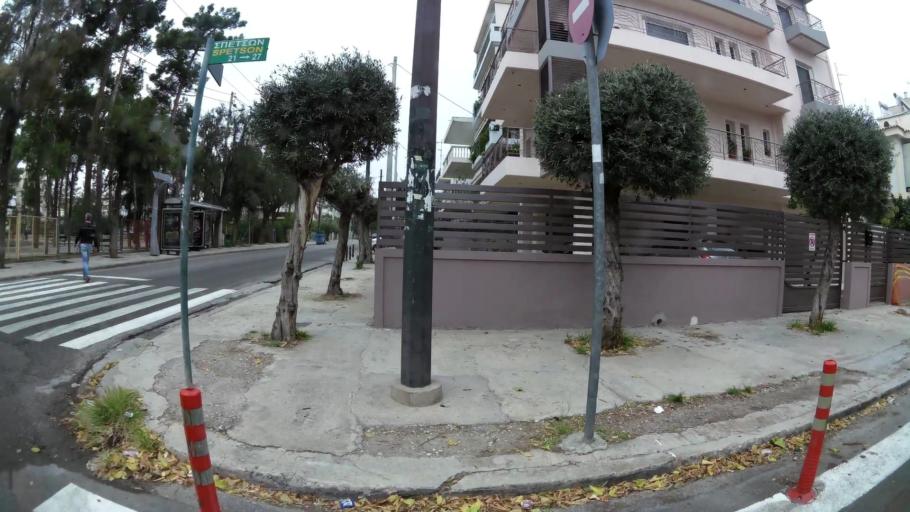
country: GR
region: Attica
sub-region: Nomarchia Athinas
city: Peristeri
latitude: 38.0130
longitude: 23.7029
